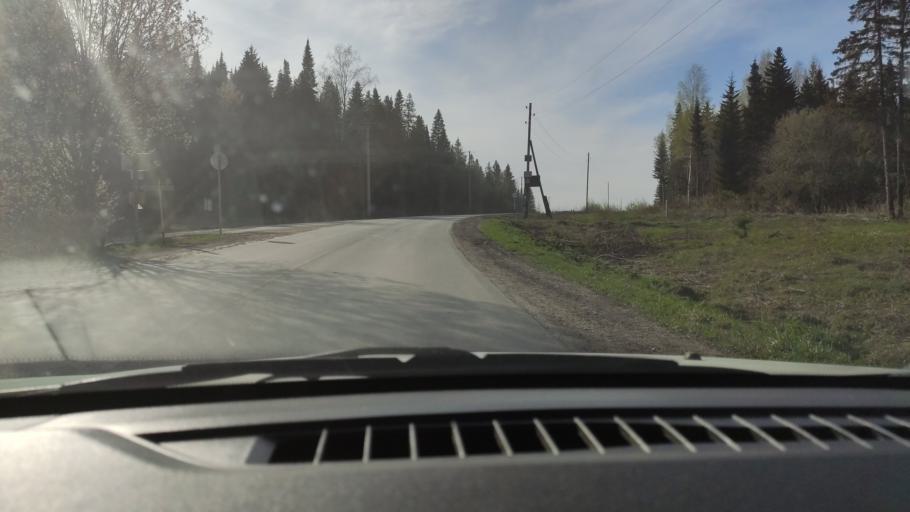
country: RU
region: Perm
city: Novyye Lyady
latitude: 57.9219
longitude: 56.6589
